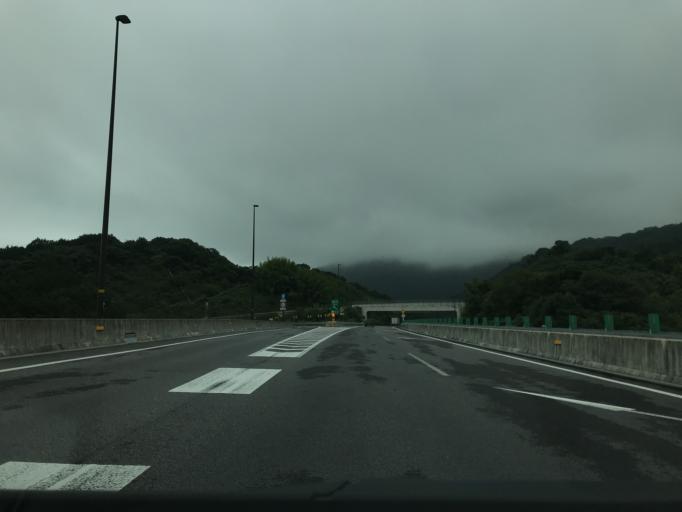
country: JP
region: Oita
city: Bungo-Takada-shi
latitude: 33.4995
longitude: 131.3163
